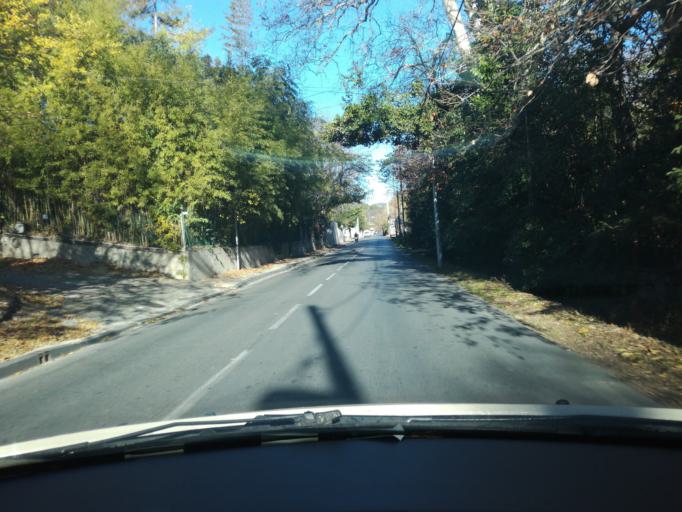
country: FR
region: Provence-Alpes-Cote d'Azur
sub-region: Departement des Bouches-du-Rhone
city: La Penne-sur-Huveaune
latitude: 43.3010
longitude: 5.5014
